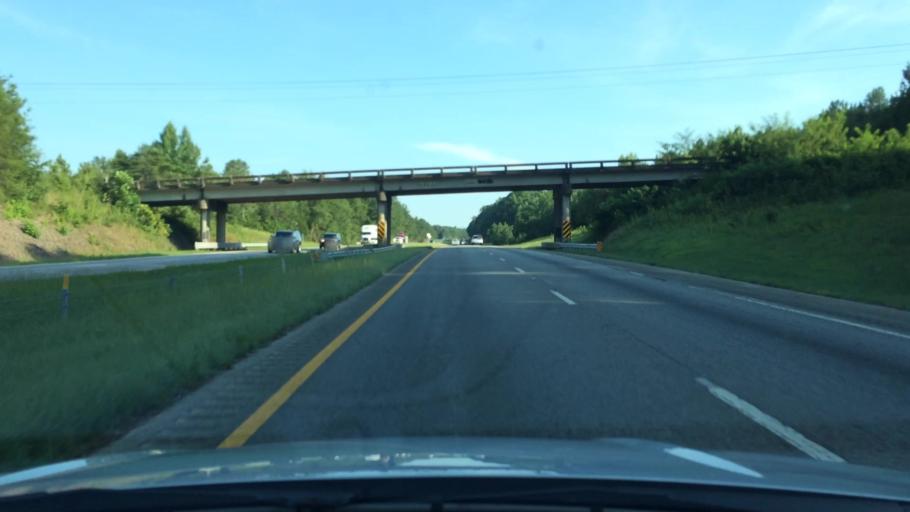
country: US
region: South Carolina
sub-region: Spartanburg County
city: Roebuck
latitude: 34.7876
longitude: -81.9556
